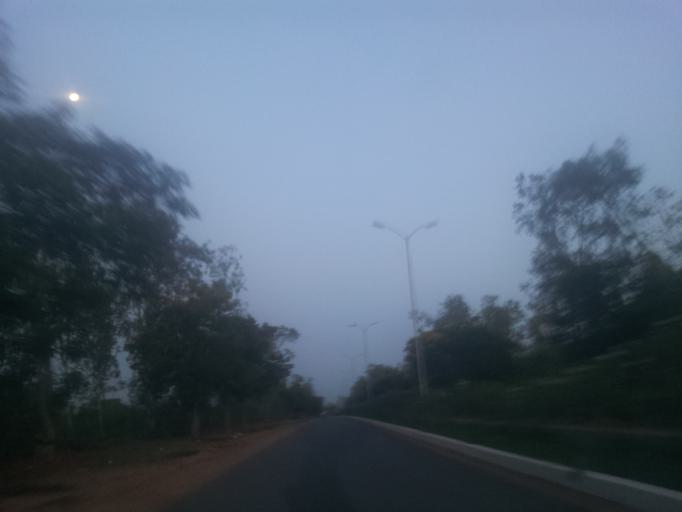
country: IN
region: Tamil Nadu
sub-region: Cuddalore
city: Kurinjippadi
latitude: 11.6219
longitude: 79.5472
